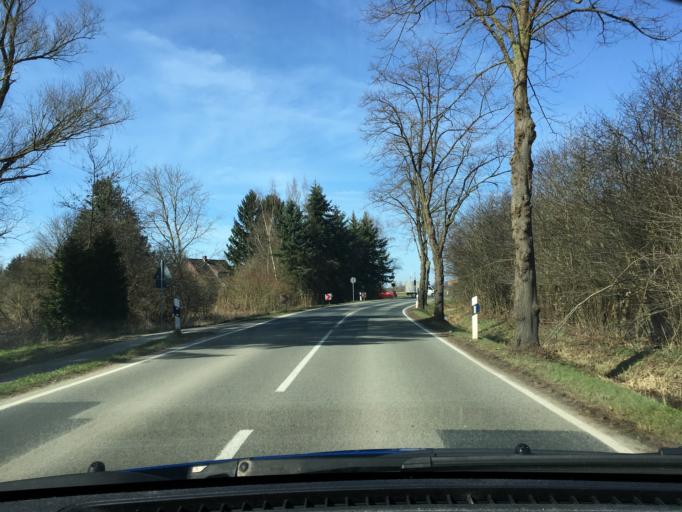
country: DE
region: Lower Saxony
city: Drage
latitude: 53.3835
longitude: 10.2440
